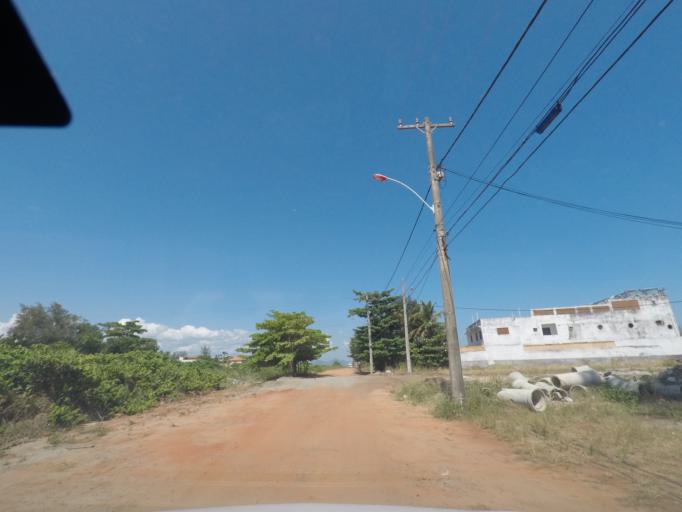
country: BR
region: Rio de Janeiro
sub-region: Marica
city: Marica
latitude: -22.9706
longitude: -42.9095
